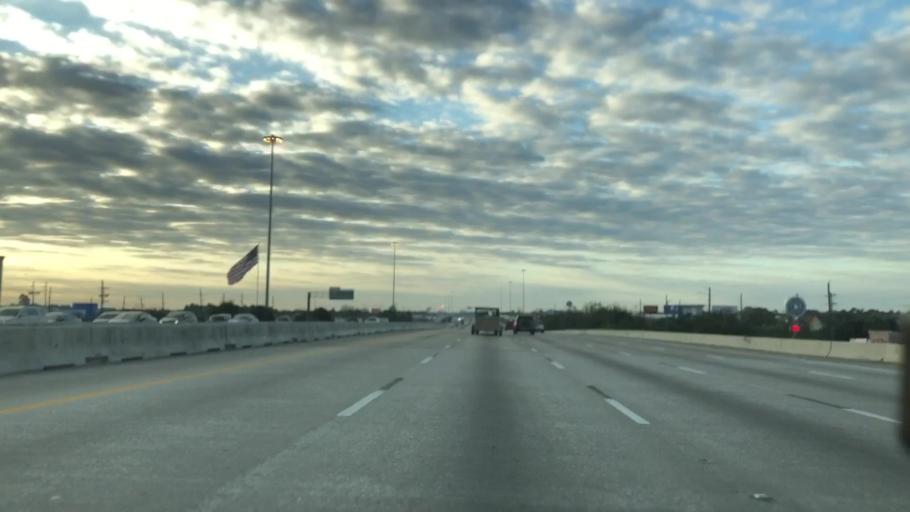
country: US
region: Texas
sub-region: Harris County
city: Spring
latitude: 30.0210
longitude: -95.4290
